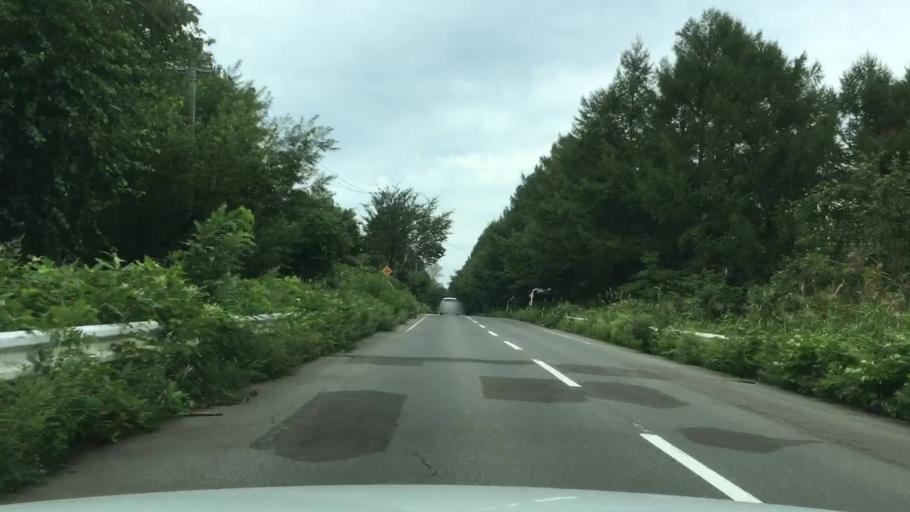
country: JP
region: Aomori
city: Shimokizukuri
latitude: 40.7140
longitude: 140.3214
